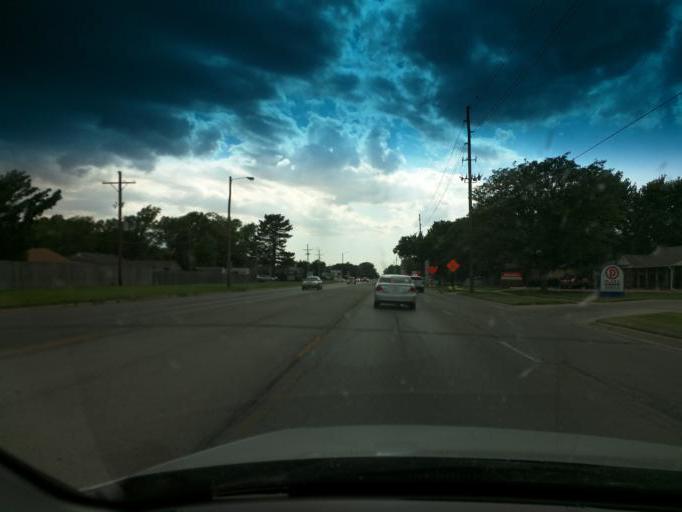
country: US
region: Kansas
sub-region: Reno County
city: Hutchinson
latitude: 38.0866
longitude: -97.9262
